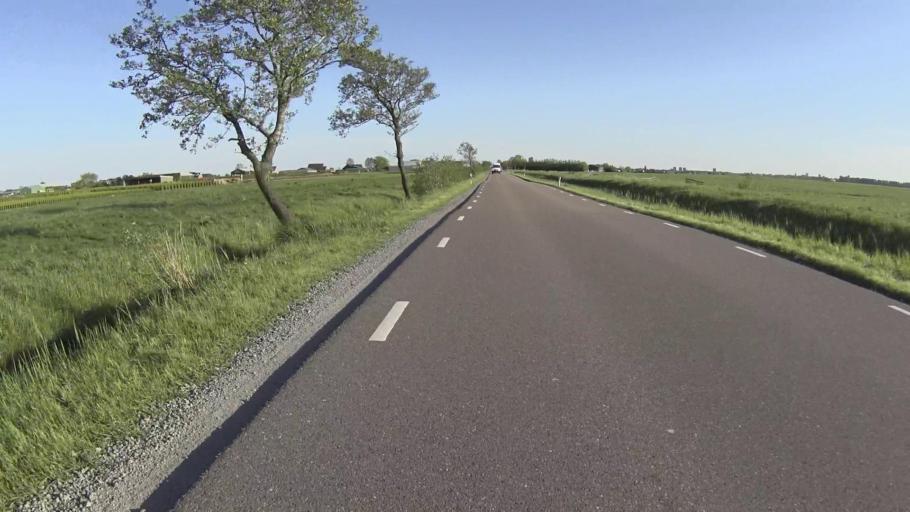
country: NL
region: South Holland
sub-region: Gemeente Rijnwoude
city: Benthuizen
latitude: 52.1089
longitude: 4.5360
